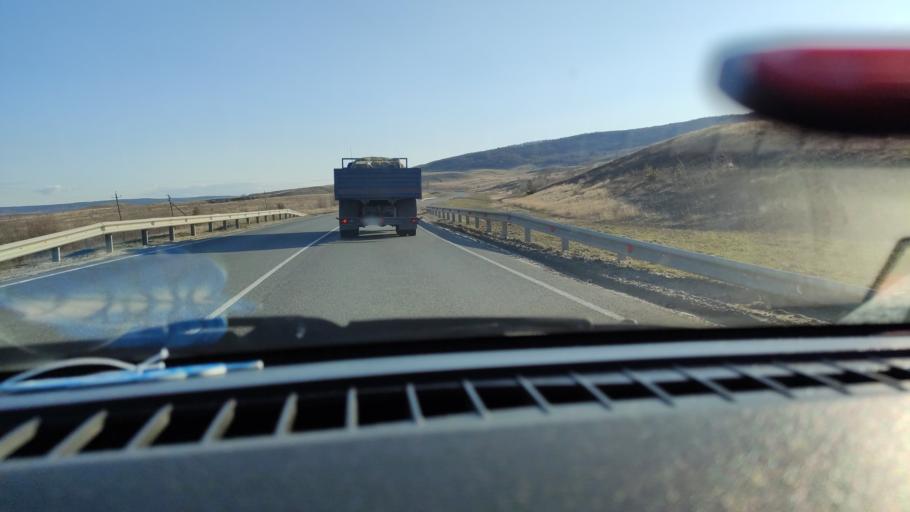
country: RU
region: Saratov
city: Alekseyevka
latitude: 52.3327
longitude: 47.9242
